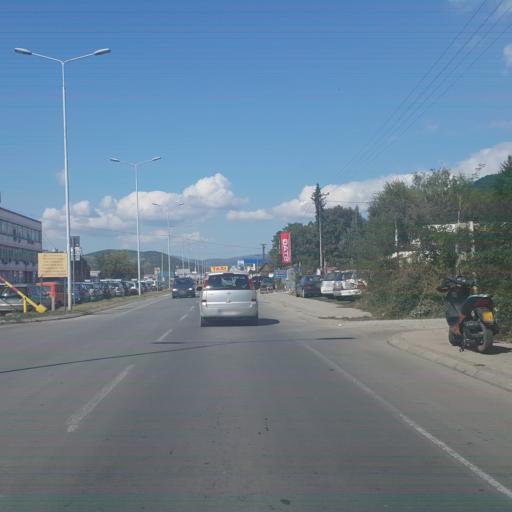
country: RS
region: Central Serbia
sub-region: Pirotski Okrug
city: Pirot
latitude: 43.1754
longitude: 22.5804
